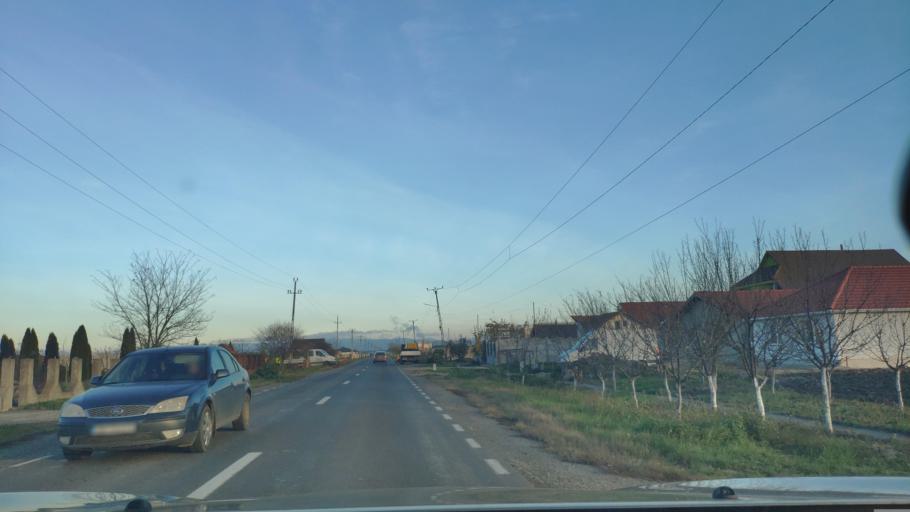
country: RO
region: Satu Mare
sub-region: Comuna Odoreu
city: Odoreu
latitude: 47.7931
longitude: 23.0092
